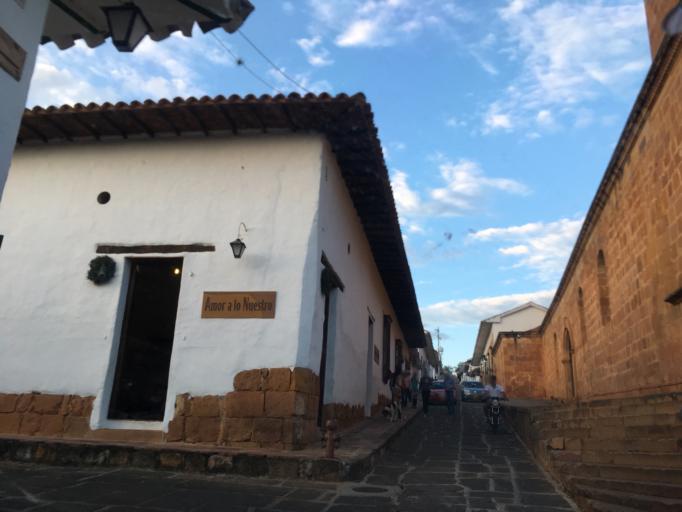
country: CO
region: Santander
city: Barichara
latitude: 6.6361
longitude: -73.2238
